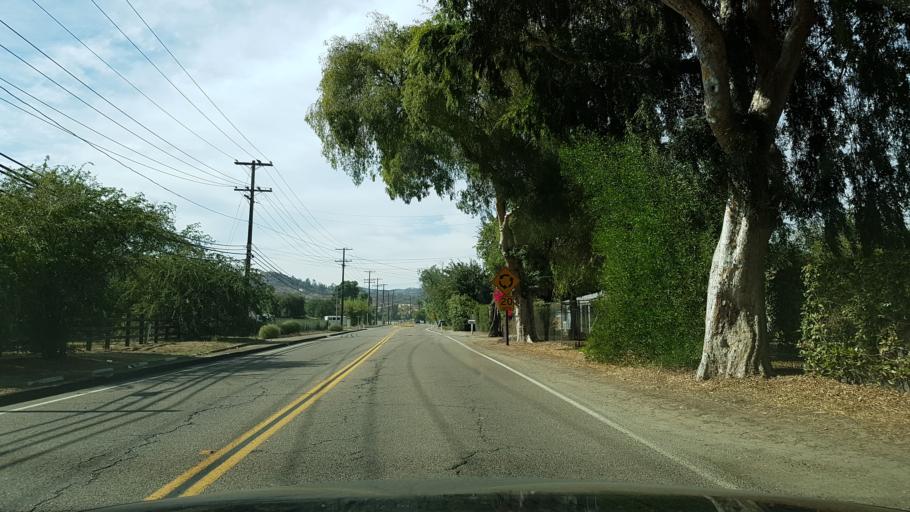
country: US
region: California
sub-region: San Diego County
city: Lakeside
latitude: 32.8758
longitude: -116.9130
